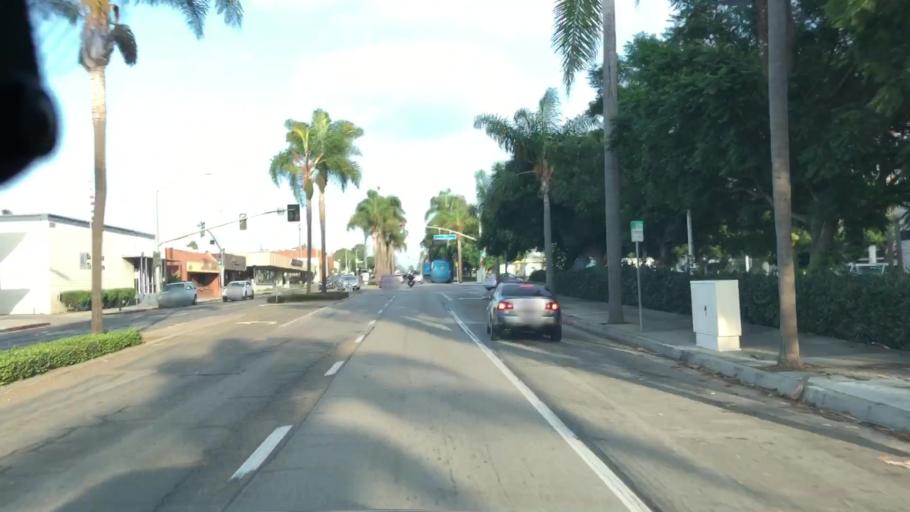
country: US
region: California
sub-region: Ventura County
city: Ventura
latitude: 34.2726
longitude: -119.2510
